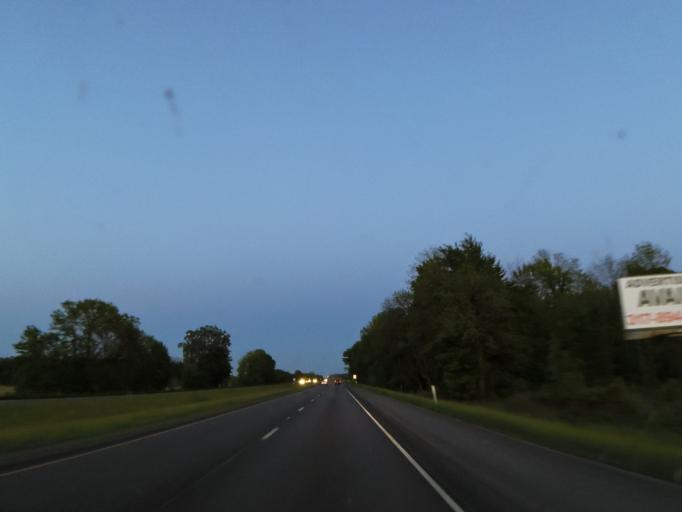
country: US
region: Indiana
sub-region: Hendricks County
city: Pittsboro
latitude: 39.8869
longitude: -86.5255
